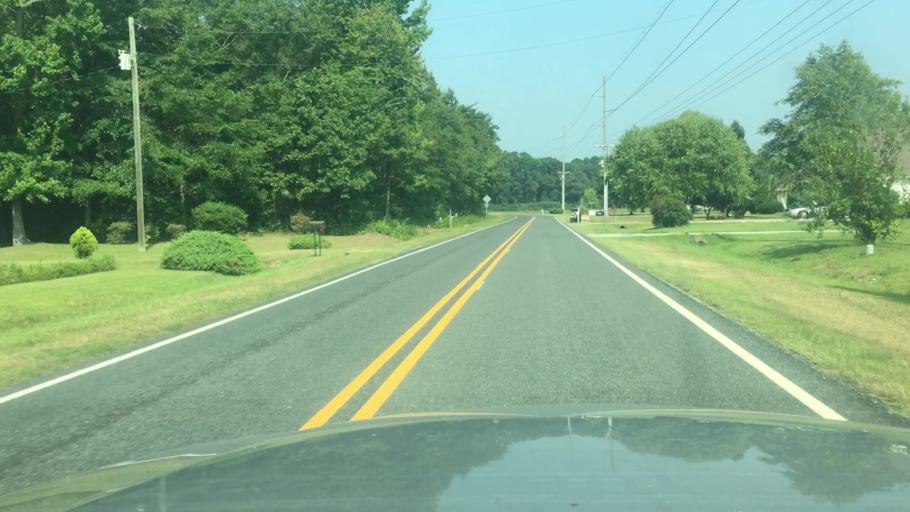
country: US
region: North Carolina
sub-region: Cumberland County
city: Hope Mills
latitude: 34.8977
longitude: -78.8914
